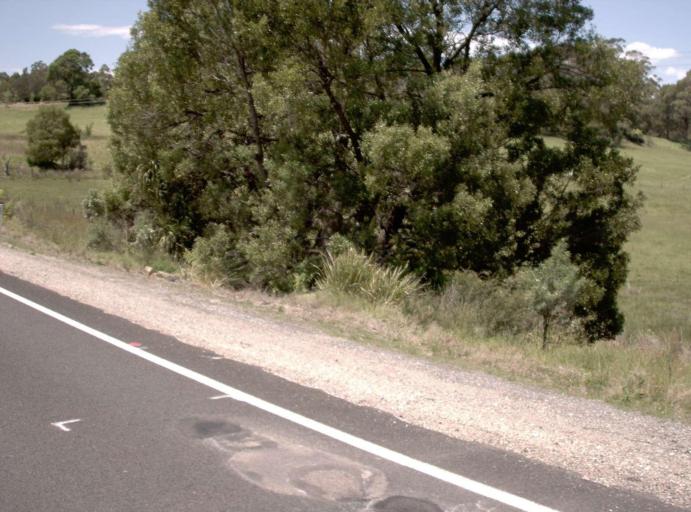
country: AU
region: Victoria
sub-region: East Gippsland
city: Lakes Entrance
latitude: -37.7005
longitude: 148.7172
